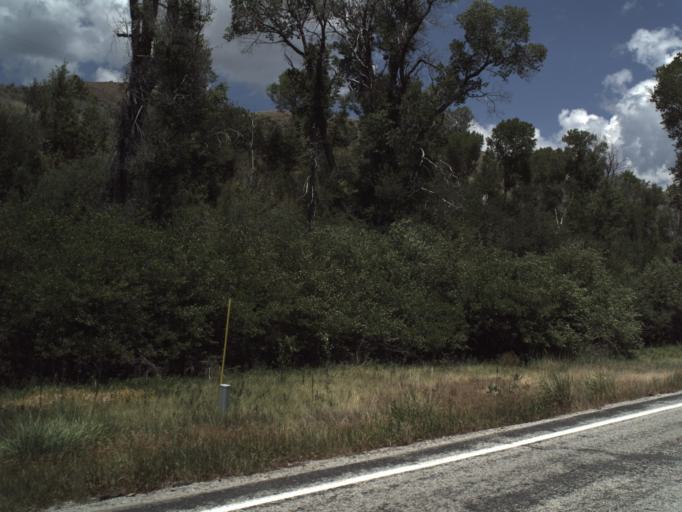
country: US
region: Utah
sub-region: Weber County
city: Wolf Creek
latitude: 41.2892
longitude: -111.6422
